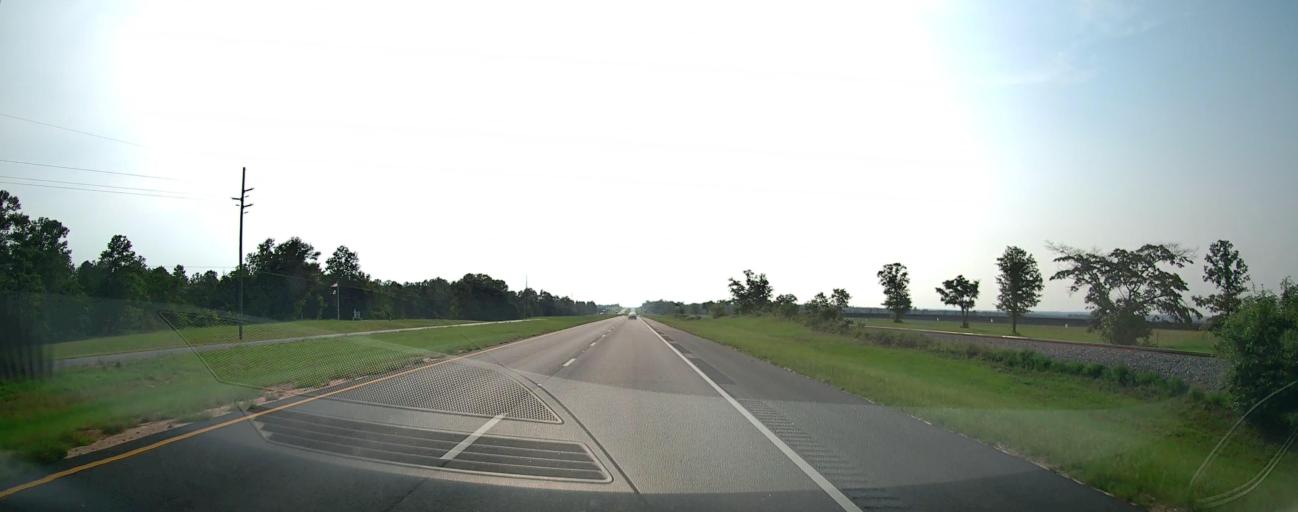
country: US
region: Georgia
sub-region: Taylor County
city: Butler
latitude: 32.5729
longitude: -84.2933
